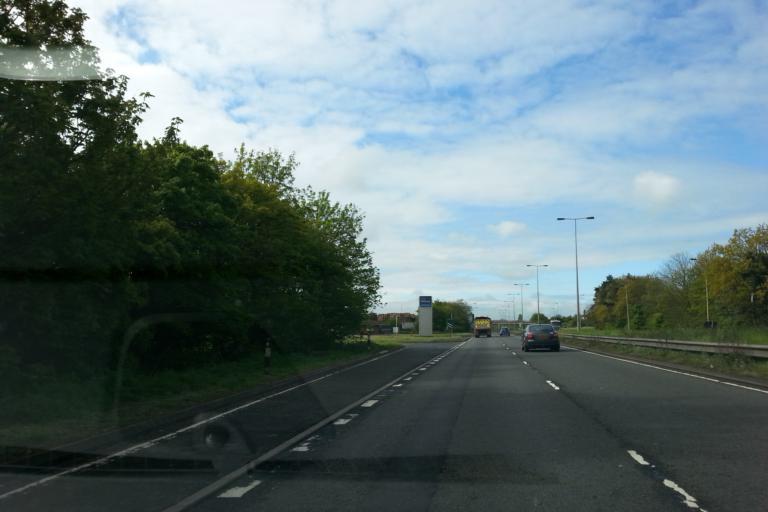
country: GB
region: England
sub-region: Staffordshire
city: Barton under Needwood
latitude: 52.7652
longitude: -1.6962
